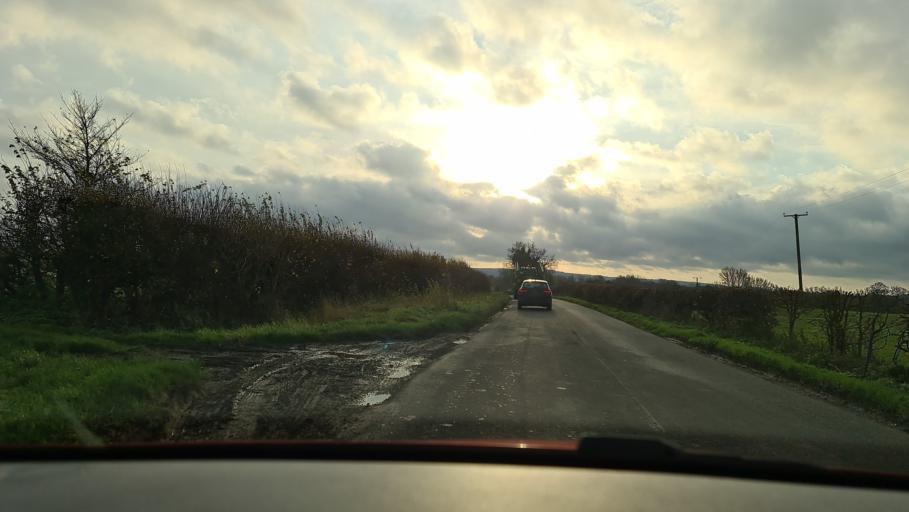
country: GB
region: England
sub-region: Buckinghamshire
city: Stone
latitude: 51.7815
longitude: -0.8794
